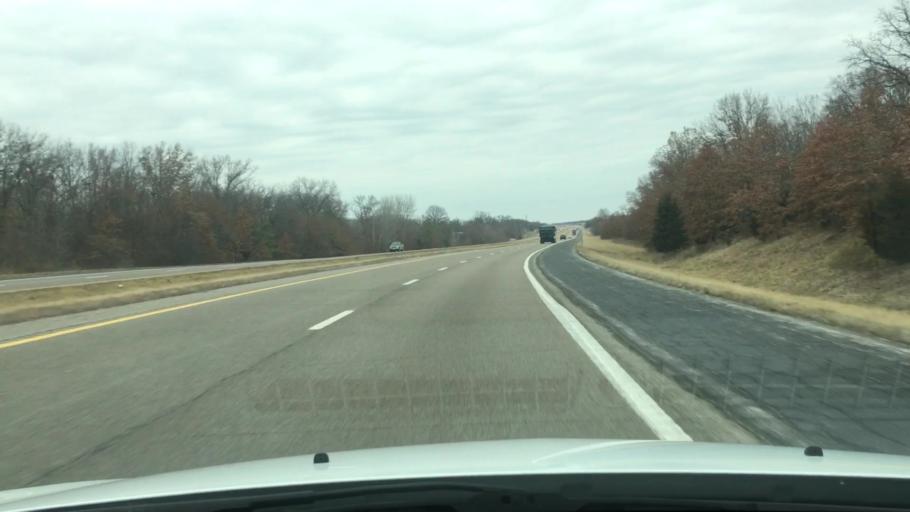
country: US
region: Missouri
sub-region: Audrain County
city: Mexico
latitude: 39.0422
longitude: -91.8932
